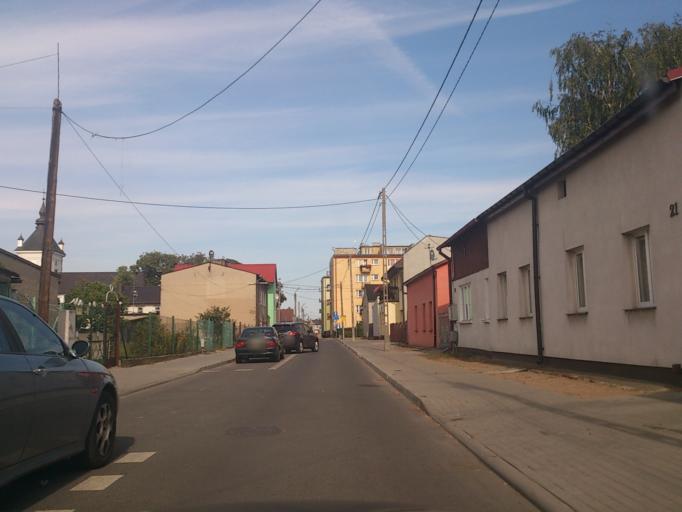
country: PL
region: Kujawsko-Pomorskie
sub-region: Powiat golubsko-dobrzynski
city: Golub-Dobrzyn
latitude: 53.1070
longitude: 19.0517
